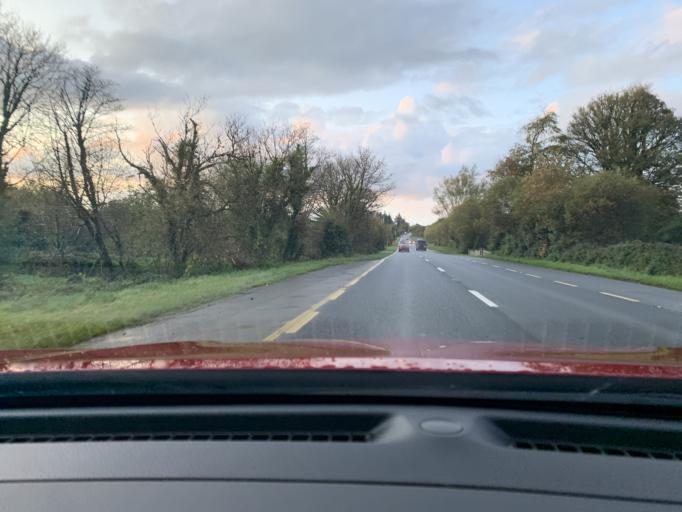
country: IE
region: Connaught
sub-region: Sligo
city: Ballymote
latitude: 54.0838
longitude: -8.3818
